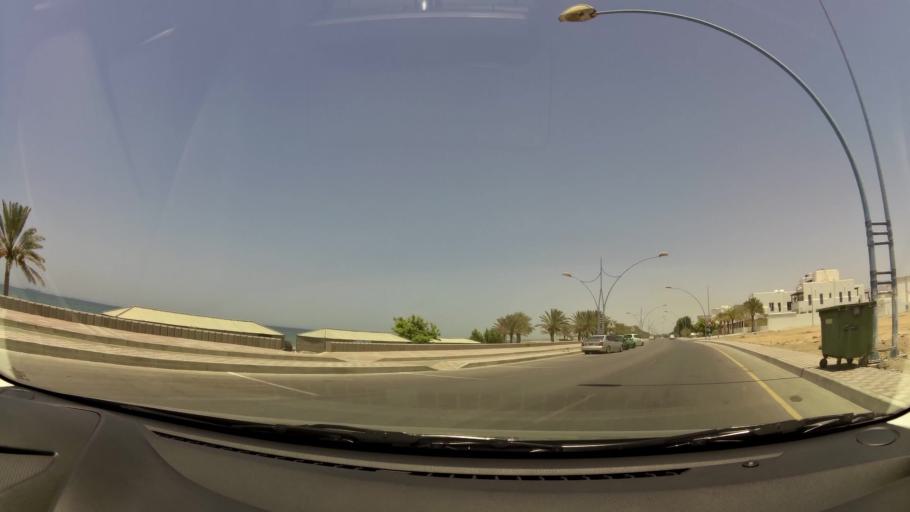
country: OM
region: Muhafazat Masqat
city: Bawshar
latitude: 23.6032
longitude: 58.3859
